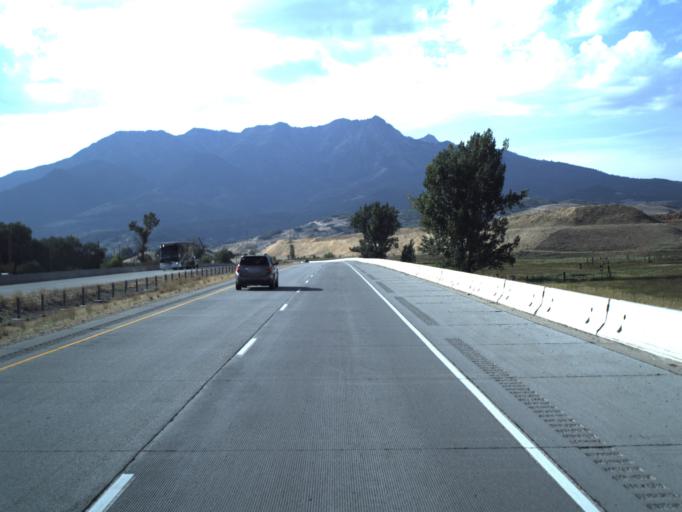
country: US
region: Utah
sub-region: Morgan County
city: Mountain Green
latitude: 41.1346
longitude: -111.7834
